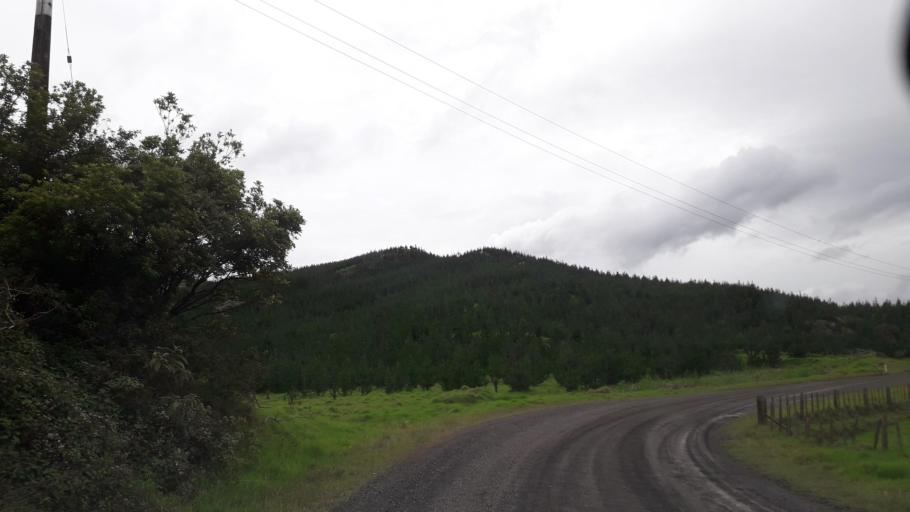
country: NZ
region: Northland
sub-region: Far North District
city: Ahipara
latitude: -35.4316
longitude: 173.3474
